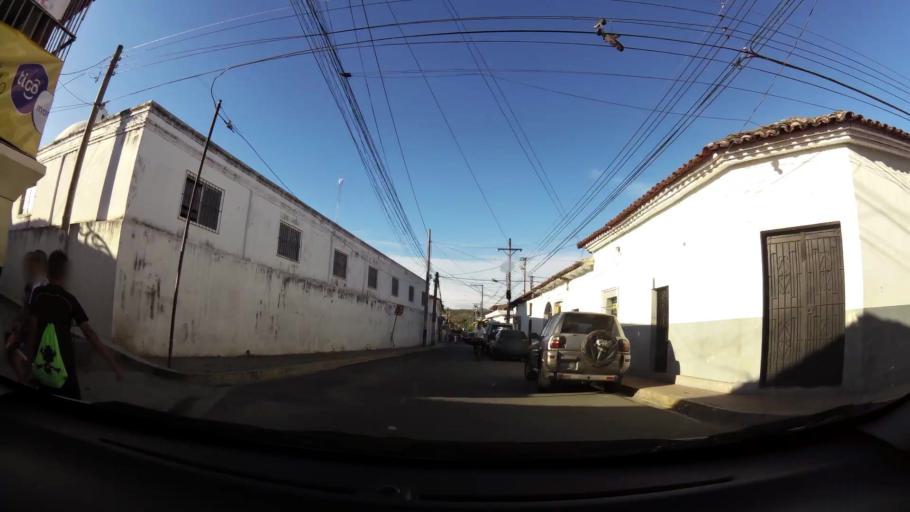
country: SV
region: Santa Ana
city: Metapan
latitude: 14.3319
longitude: -89.4469
